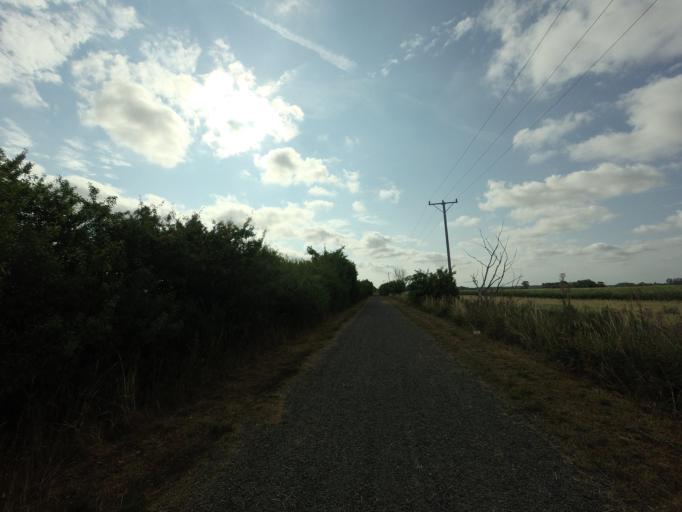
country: SE
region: Skane
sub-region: Angelholms Kommun
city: Strovelstorp
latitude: 56.1528
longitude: 12.7629
